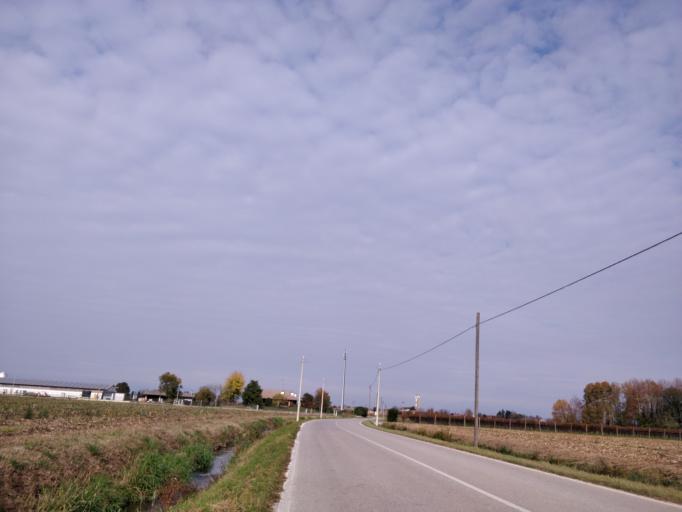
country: IT
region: Friuli Venezia Giulia
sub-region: Provincia di Udine
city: Bertiolo
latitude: 45.9335
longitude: 13.0506
